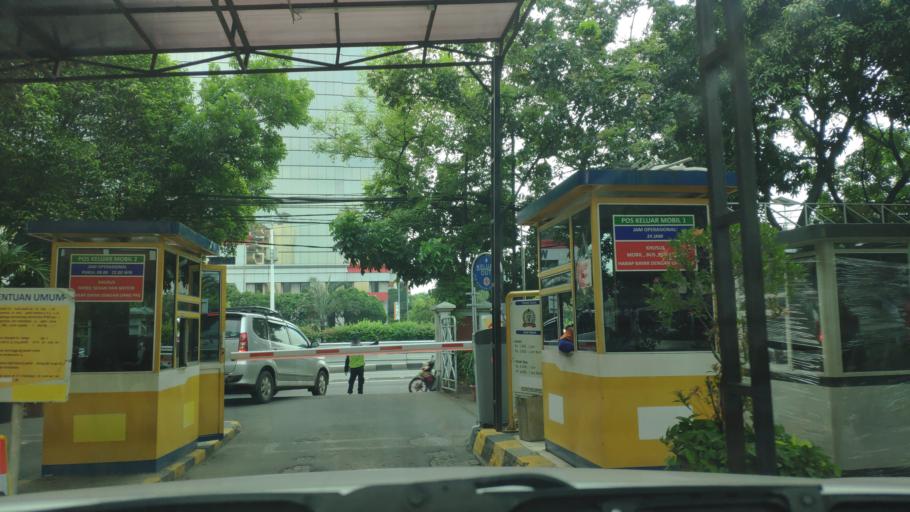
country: ID
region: Jakarta Raya
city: Jakarta
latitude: -6.1865
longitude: 106.7974
